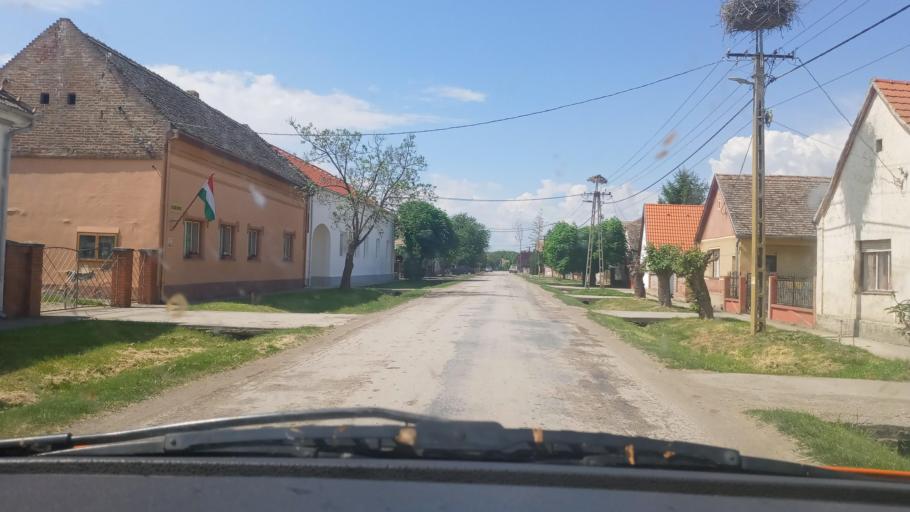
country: HU
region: Baranya
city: Beremend
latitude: 45.7878
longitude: 18.3532
